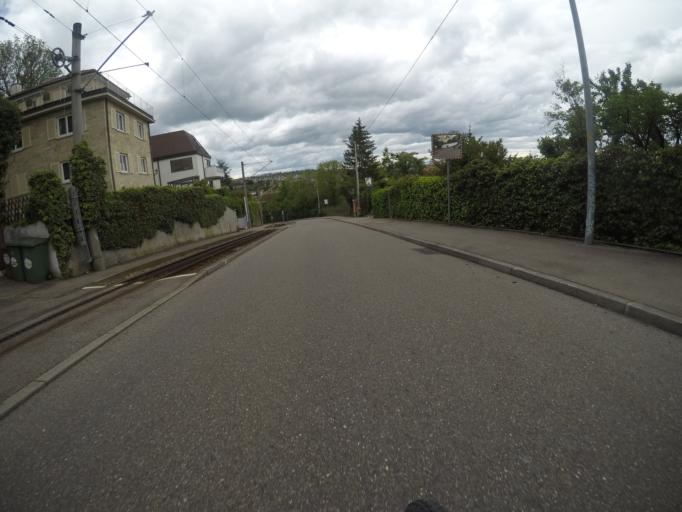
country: DE
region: Baden-Wuerttemberg
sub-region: Regierungsbezirk Stuttgart
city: Stuttgart
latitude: 48.7594
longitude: 9.1685
